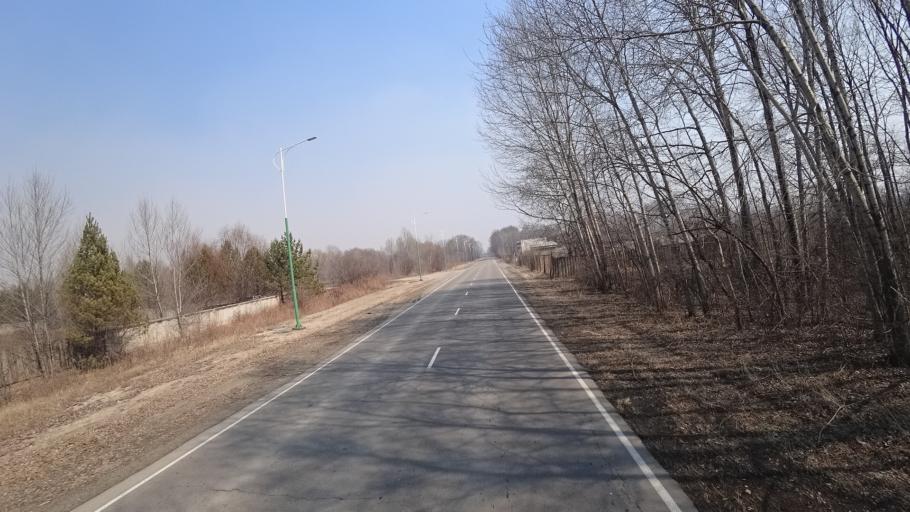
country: RU
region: Amur
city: Novobureyskiy
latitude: 49.7835
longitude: 129.9276
